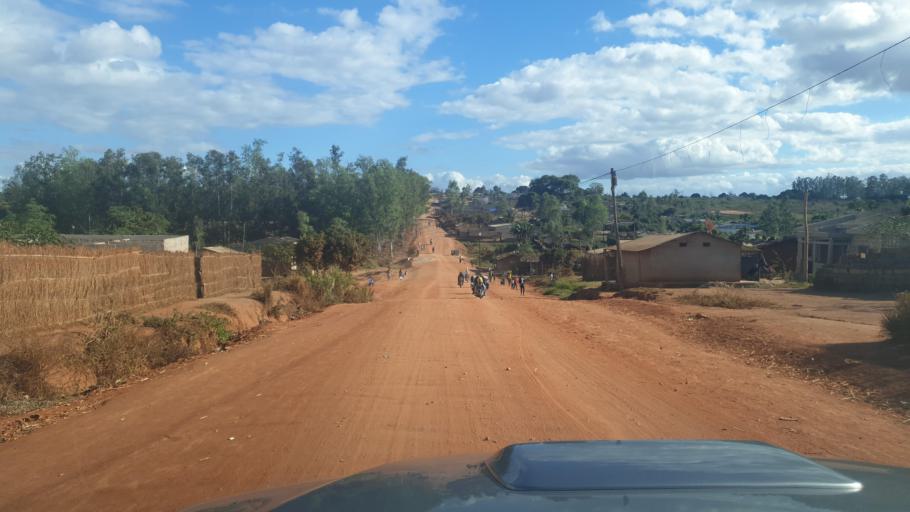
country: MZ
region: Nampula
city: Nampula
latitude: -15.0964
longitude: 39.2253
